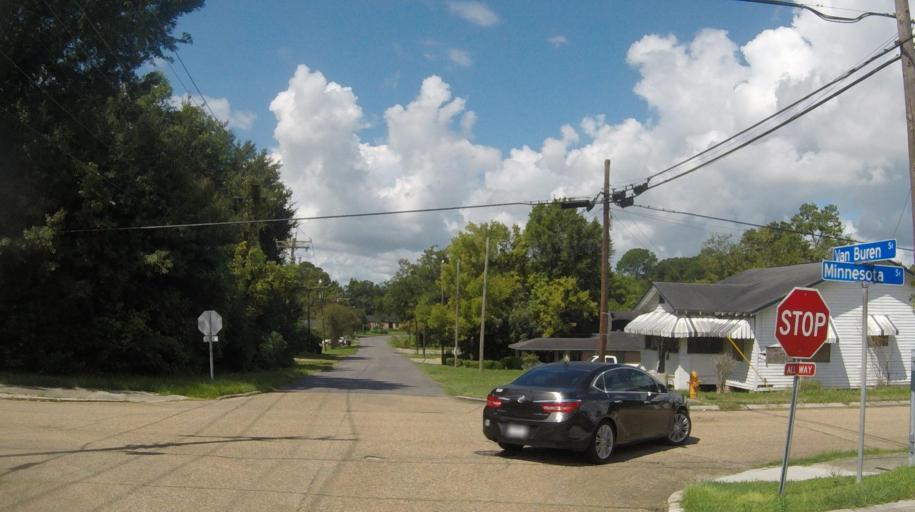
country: US
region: Louisiana
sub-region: West Baton Rouge Parish
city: Port Allen
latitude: 30.4297
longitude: -91.1834
